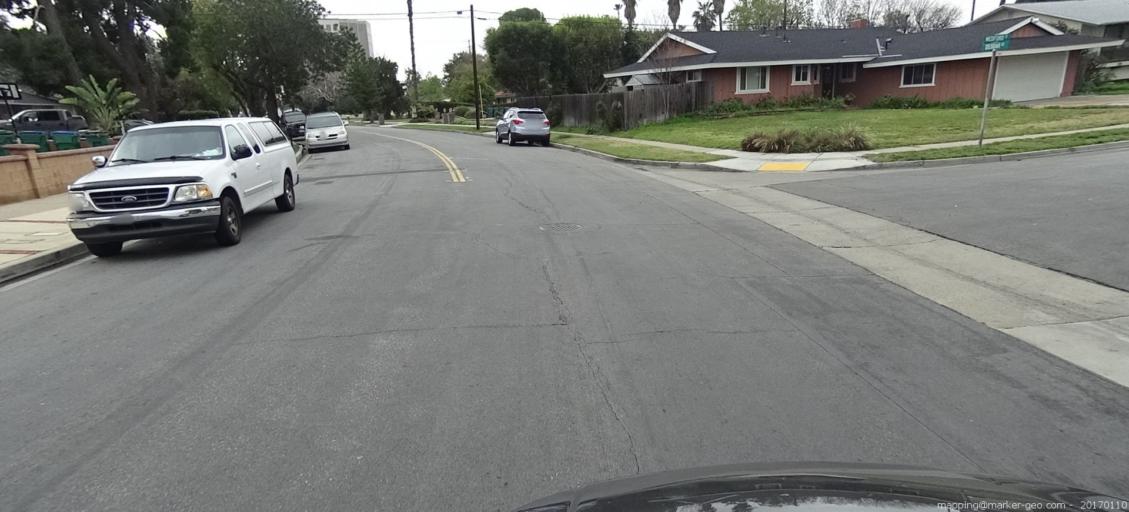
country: US
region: California
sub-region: Orange County
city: Tustin
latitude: 33.7621
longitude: -117.8320
